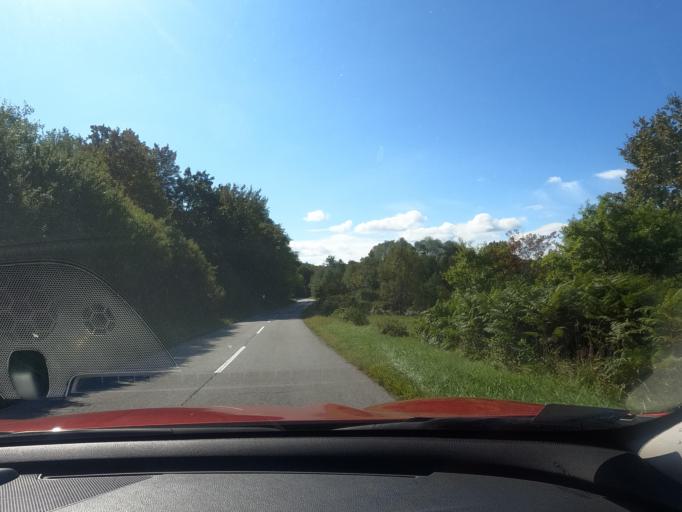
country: BA
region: Federation of Bosnia and Herzegovina
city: Vrnograc
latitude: 45.2742
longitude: 15.9728
